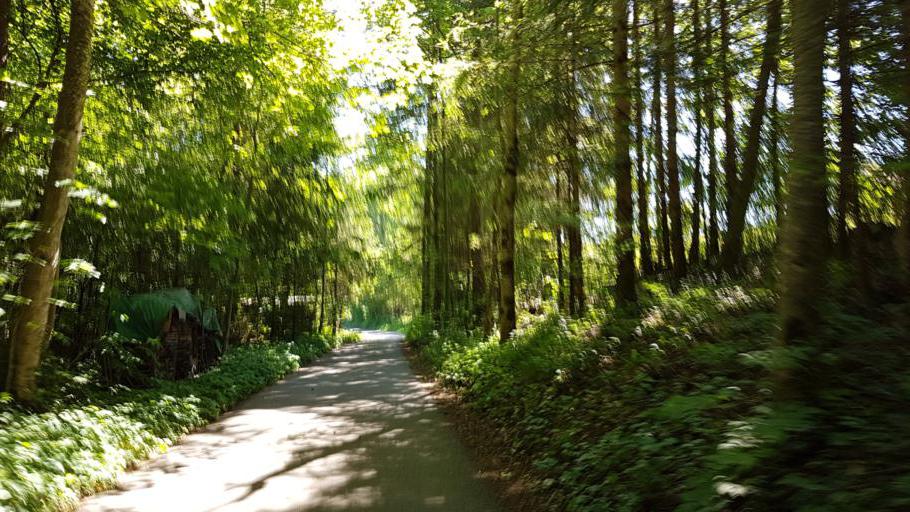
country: CH
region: Bern
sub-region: Thun District
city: Thierachern
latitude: 46.7101
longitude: 7.5779
